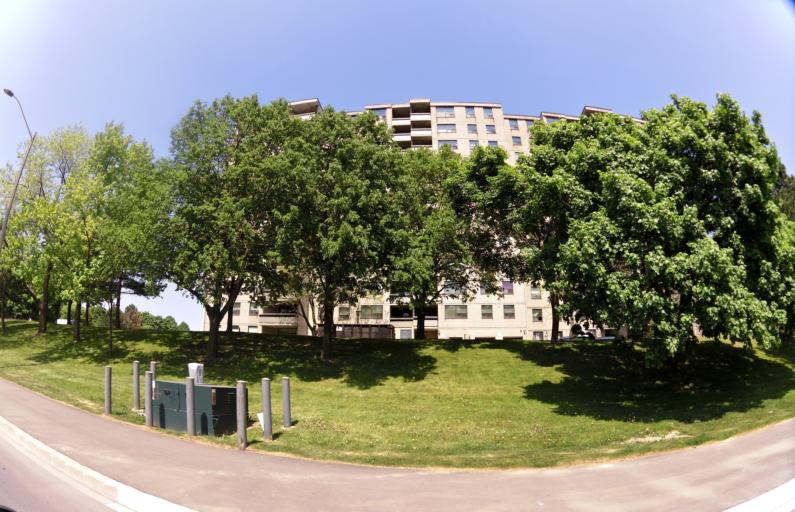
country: CA
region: Ontario
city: Mississauga
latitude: 43.6069
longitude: -79.6349
